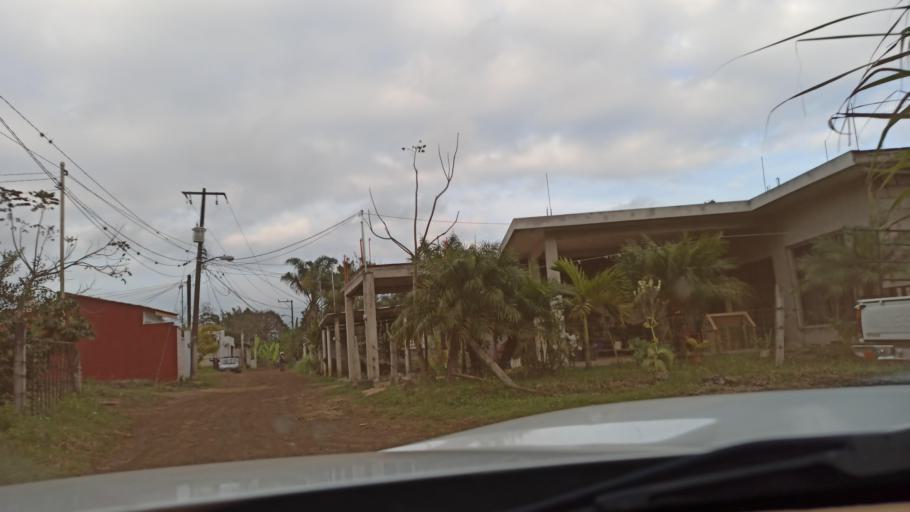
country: MX
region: Veracruz
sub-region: Fortin
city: Monte Salas
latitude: 18.9274
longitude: -97.0114
